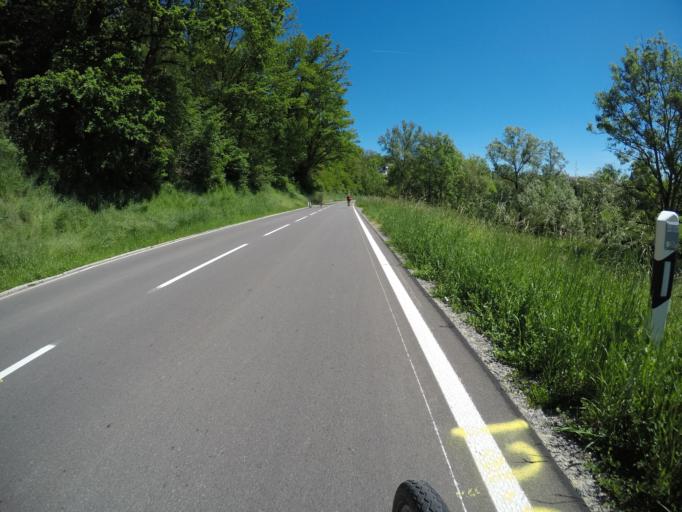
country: DE
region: Baden-Wuerttemberg
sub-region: Karlsruhe Region
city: Friolzheim
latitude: 48.8061
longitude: 8.8173
